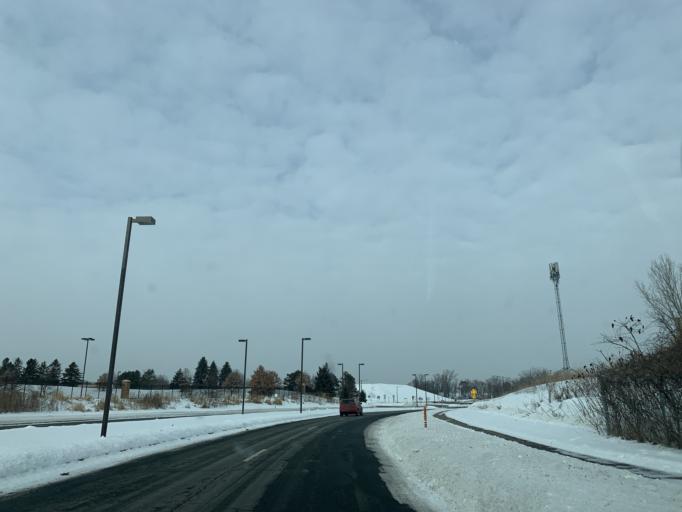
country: US
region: Minnesota
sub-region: Dakota County
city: Mendota Heights
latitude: 44.8556
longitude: -93.1235
